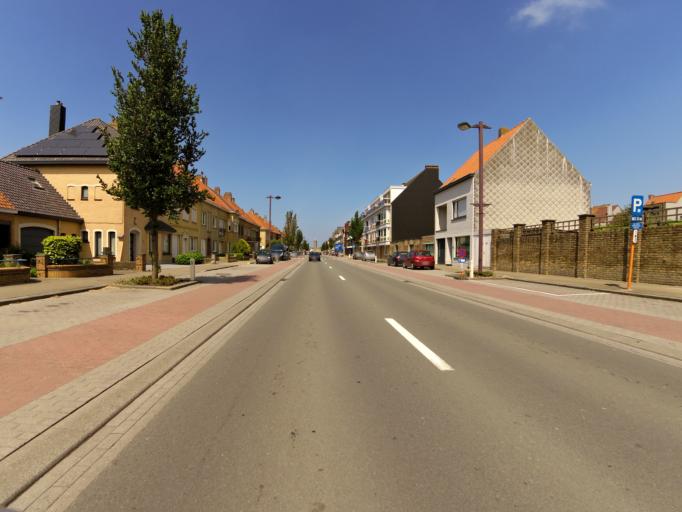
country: BE
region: Flanders
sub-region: Provincie West-Vlaanderen
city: Nieuwpoort
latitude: 51.1298
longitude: 2.7478
